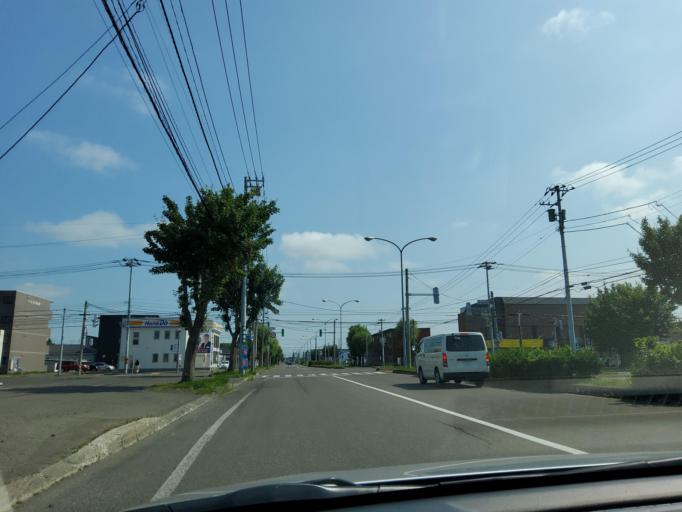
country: JP
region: Hokkaido
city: Obihiro
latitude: 42.9166
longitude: 143.1933
